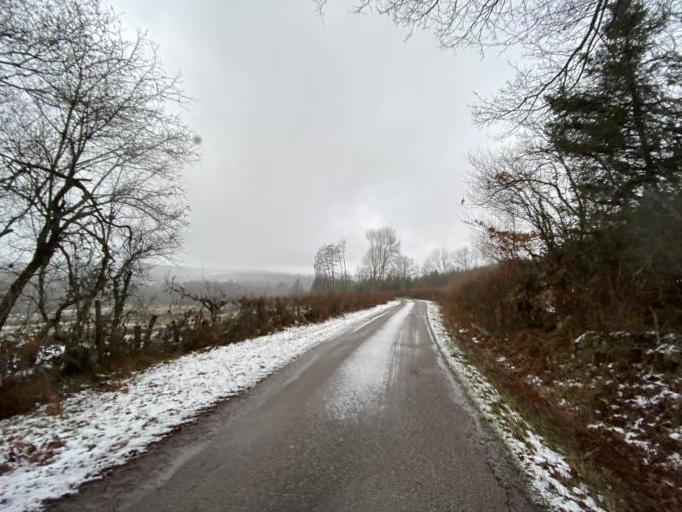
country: FR
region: Bourgogne
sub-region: Departement de la Cote-d'Or
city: Saulieu
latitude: 47.2669
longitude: 4.1597
